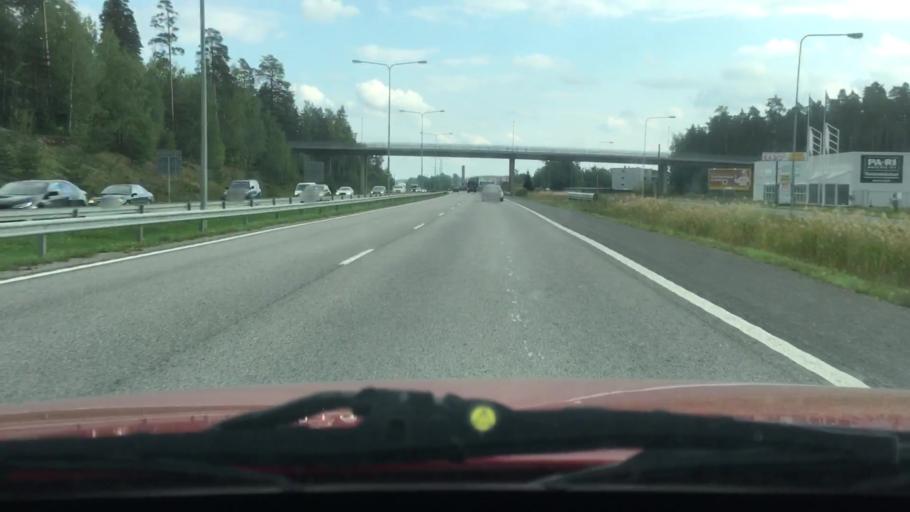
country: FI
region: Varsinais-Suomi
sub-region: Turku
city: Raisio
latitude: 60.4972
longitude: 22.1639
